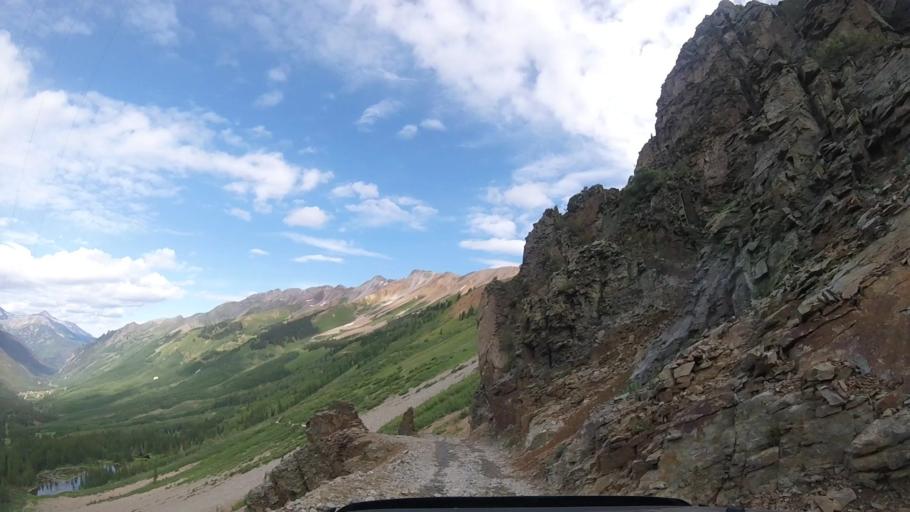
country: US
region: Colorado
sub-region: San Miguel County
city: Telluride
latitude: 37.8557
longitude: -107.7871
